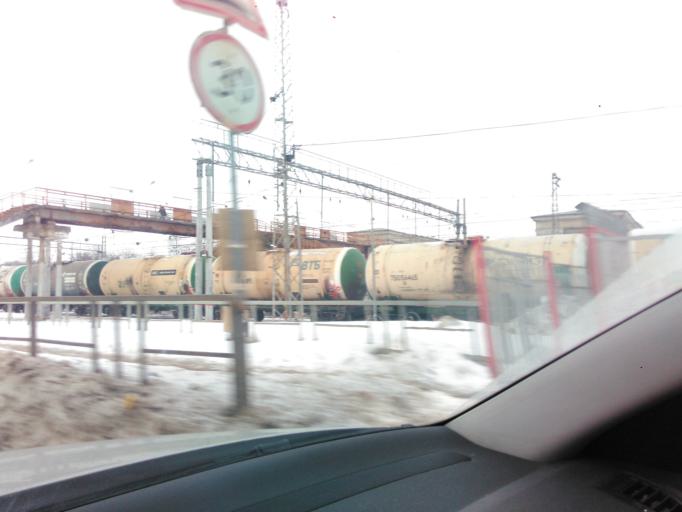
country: RU
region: Moskovskaya
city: Yakhroma
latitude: 56.2870
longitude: 37.5021
